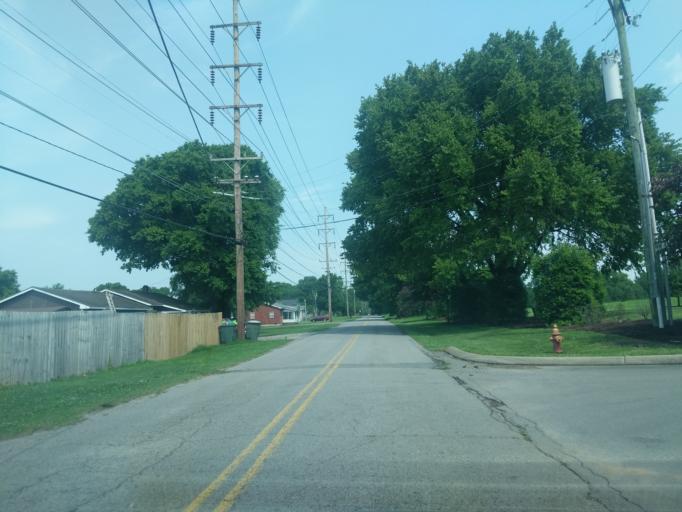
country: US
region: Tennessee
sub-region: Davidson County
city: Lakewood
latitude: 36.2782
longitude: -86.6707
